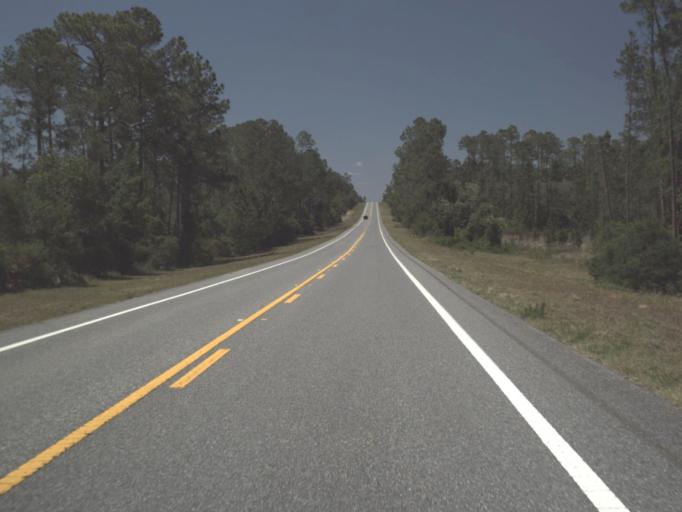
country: US
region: Florida
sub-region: Lake County
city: Astor
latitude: 29.1394
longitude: -81.6276
